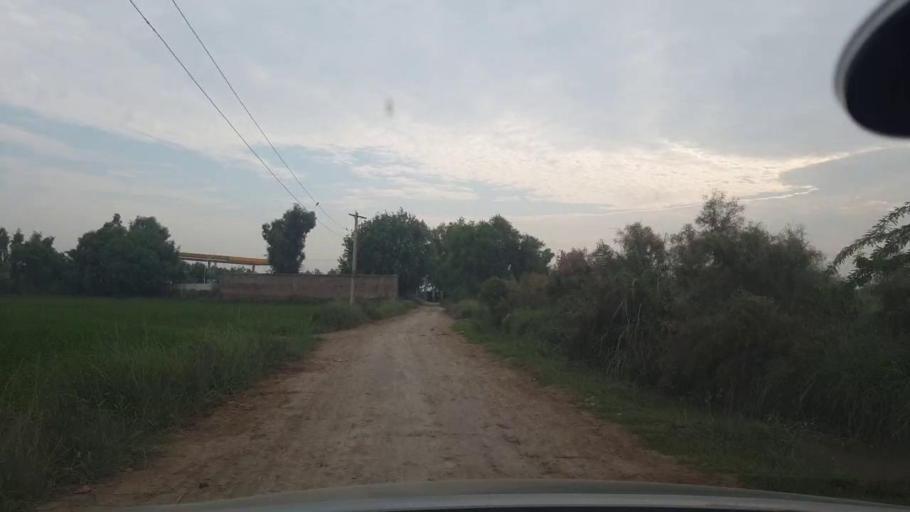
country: PK
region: Sindh
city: Jacobabad
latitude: 28.2986
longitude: 68.4254
